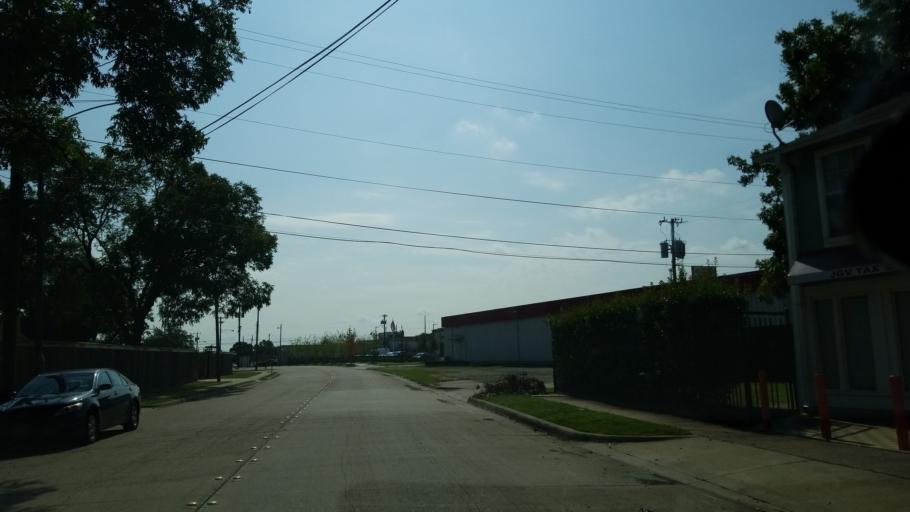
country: US
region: Texas
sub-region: Dallas County
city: Garland
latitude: 32.9136
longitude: -96.6444
